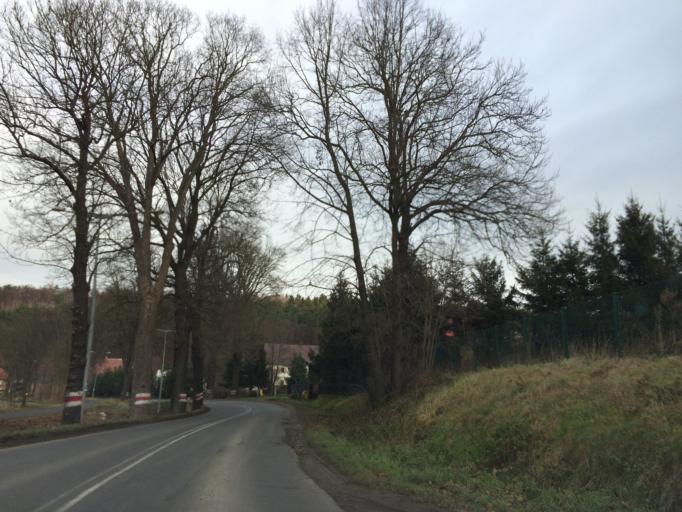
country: PL
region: Lower Silesian Voivodeship
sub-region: Powiat lwowecki
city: Lwowek Slaski
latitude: 51.0955
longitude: 15.5955
